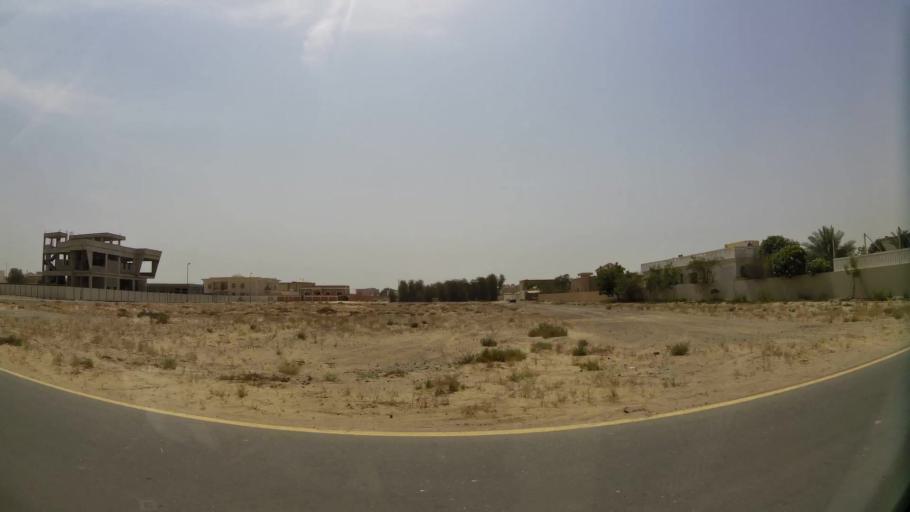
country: AE
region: Ash Shariqah
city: Sharjah
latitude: 25.2515
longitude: 55.4788
